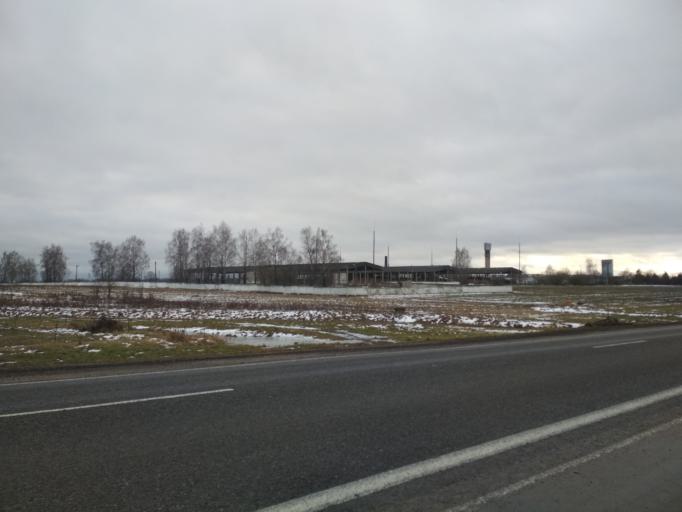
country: BY
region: Minsk
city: Mar''ina Horka
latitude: 53.5112
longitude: 28.1137
